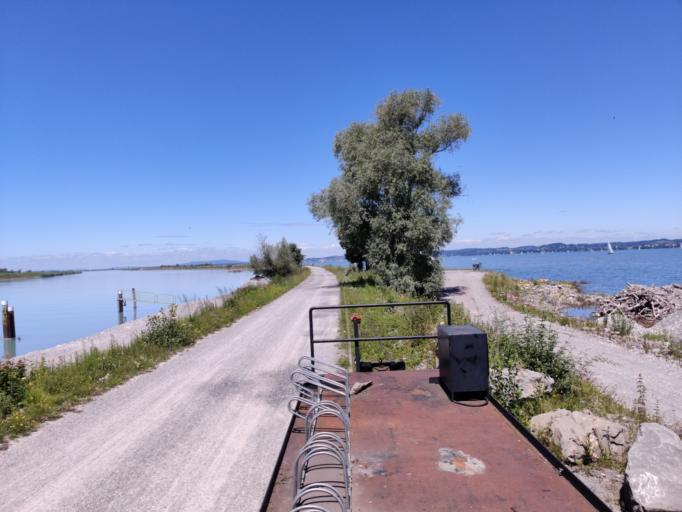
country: AT
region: Vorarlberg
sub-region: Politischer Bezirk Bregenz
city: Hard
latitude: 47.5048
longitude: 9.6704
